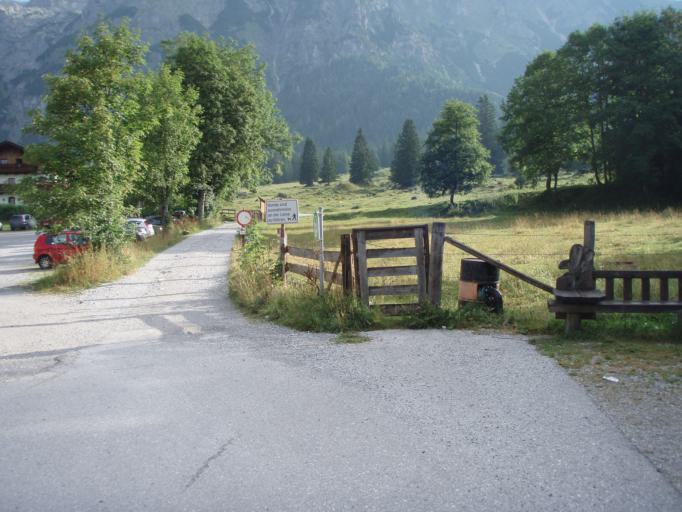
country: AT
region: Salzburg
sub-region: Politischer Bezirk Sankt Johann im Pongau
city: Werfenweng
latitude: 47.4747
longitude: 13.2689
